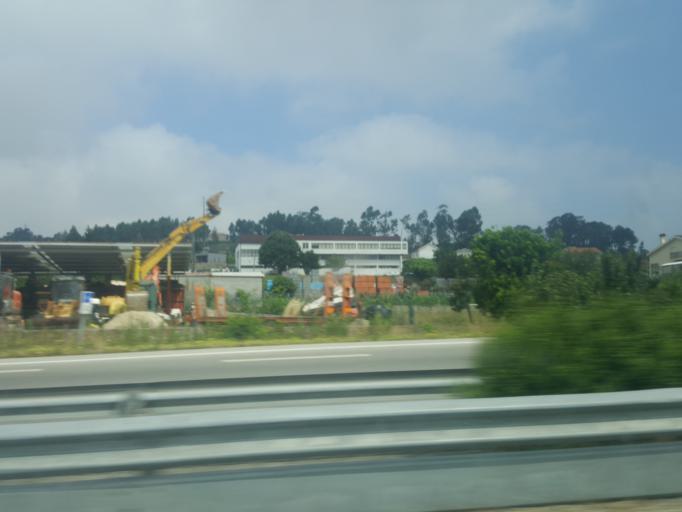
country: PT
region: Porto
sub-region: Lousada
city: Meinedo
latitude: 41.2229
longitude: -8.2362
